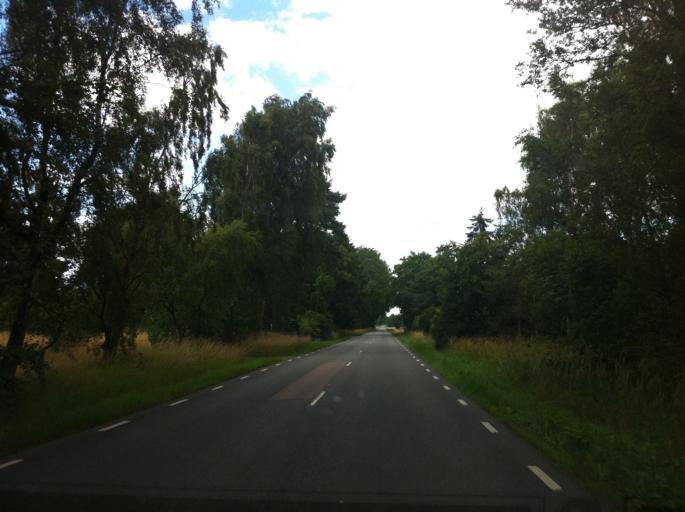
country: SE
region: Skane
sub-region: Simrishamns Kommun
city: Simrishamn
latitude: 55.4129
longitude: 14.1999
